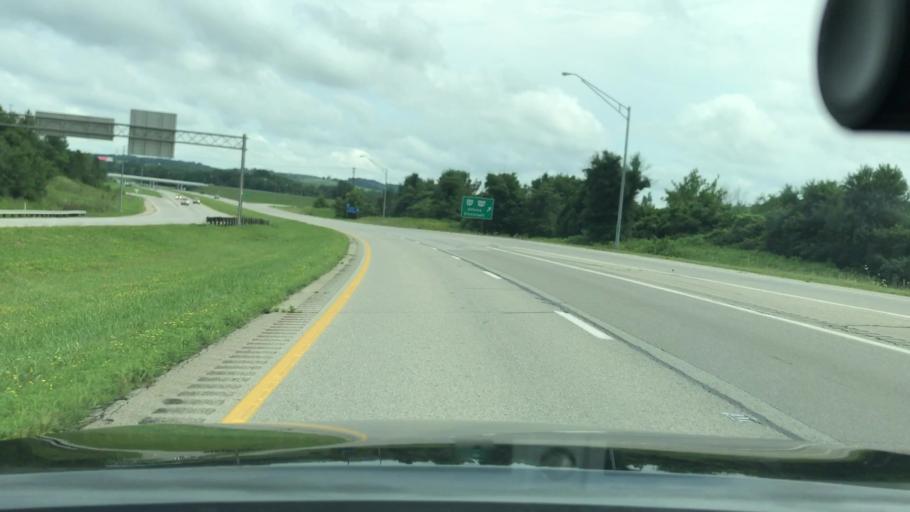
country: US
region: Ohio
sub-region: Jackson County
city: Jackson
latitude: 39.0510
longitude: -82.6181
